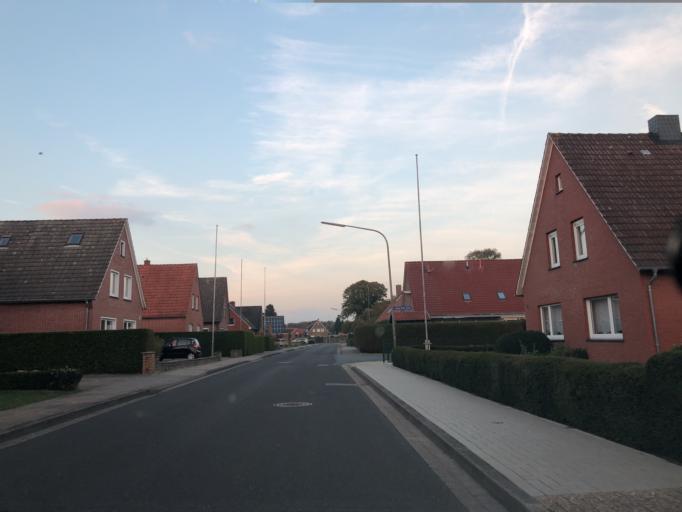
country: DE
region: Lower Saxony
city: Papenburg
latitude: 53.0697
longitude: 7.4263
